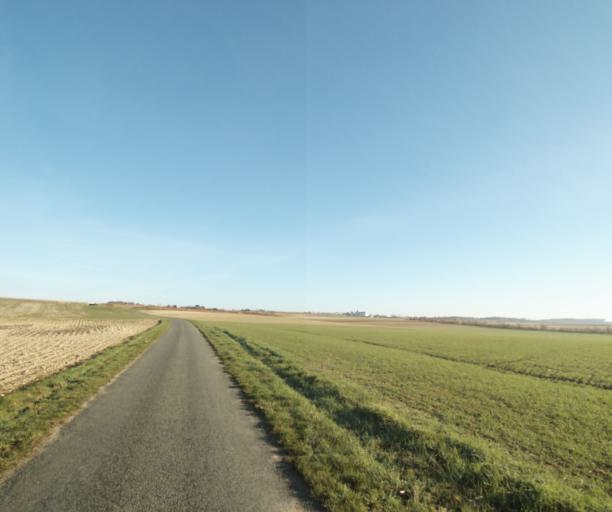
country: FR
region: Poitou-Charentes
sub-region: Departement de la Charente-Maritime
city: Cherac
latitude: 45.6956
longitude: -0.4567
